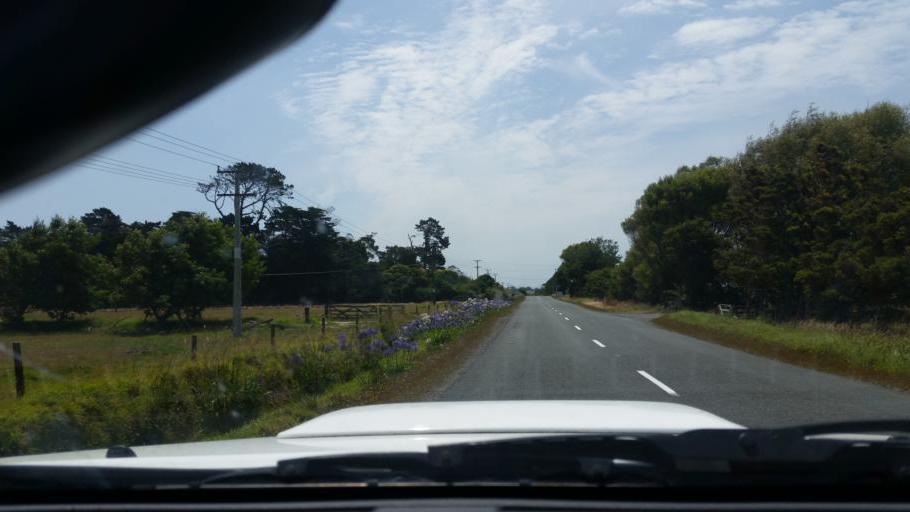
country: NZ
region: Northland
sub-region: Kaipara District
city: Dargaville
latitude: -36.0615
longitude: 173.9366
